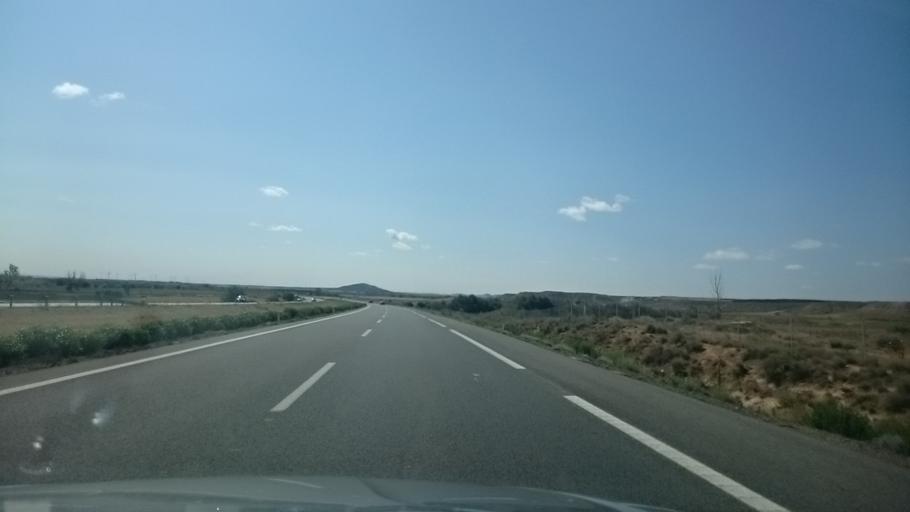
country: ES
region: Aragon
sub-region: Provincia de Zaragoza
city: Frescano
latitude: 41.9309
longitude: -1.4975
